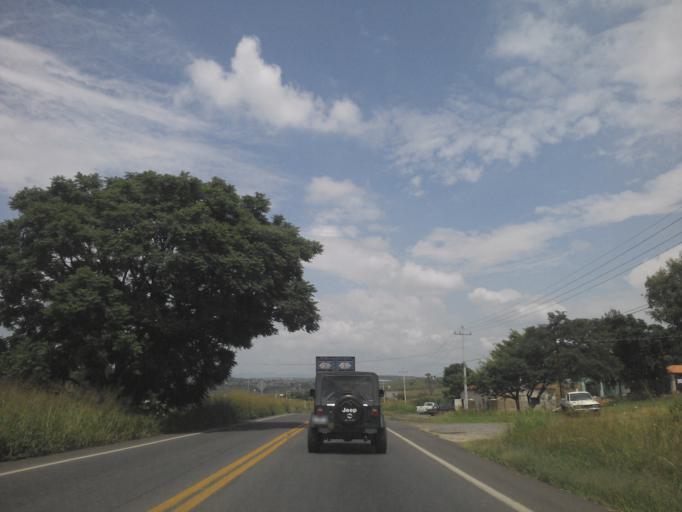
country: MX
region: Jalisco
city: Zapotlanejo
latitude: 20.6649
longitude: -103.0134
